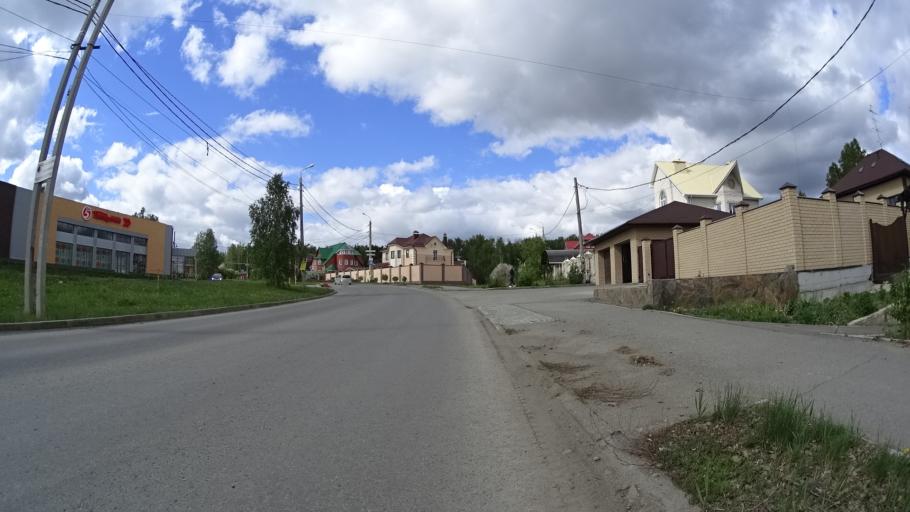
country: RU
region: Chelyabinsk
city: Sargazy
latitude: 55.1538
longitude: 61.2548
